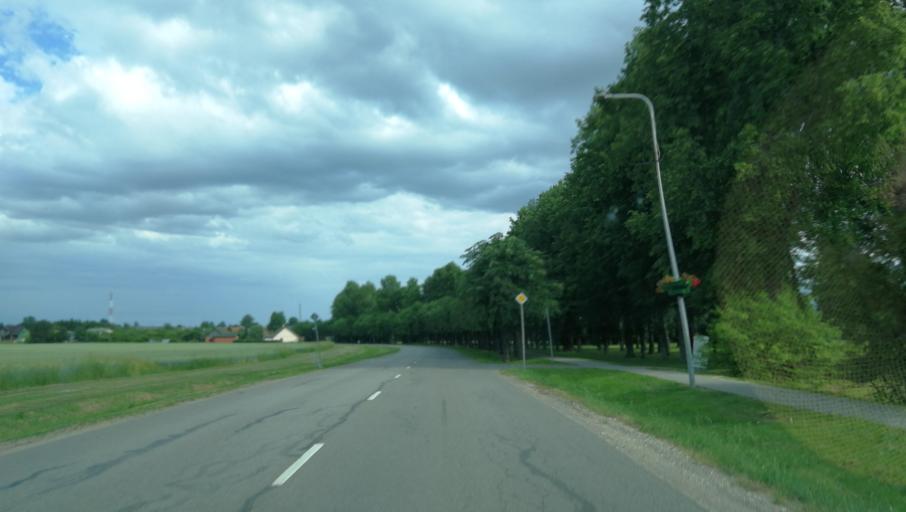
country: LV
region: Rujienas
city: Rujiena
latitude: 57.8914
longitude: 25.3446
